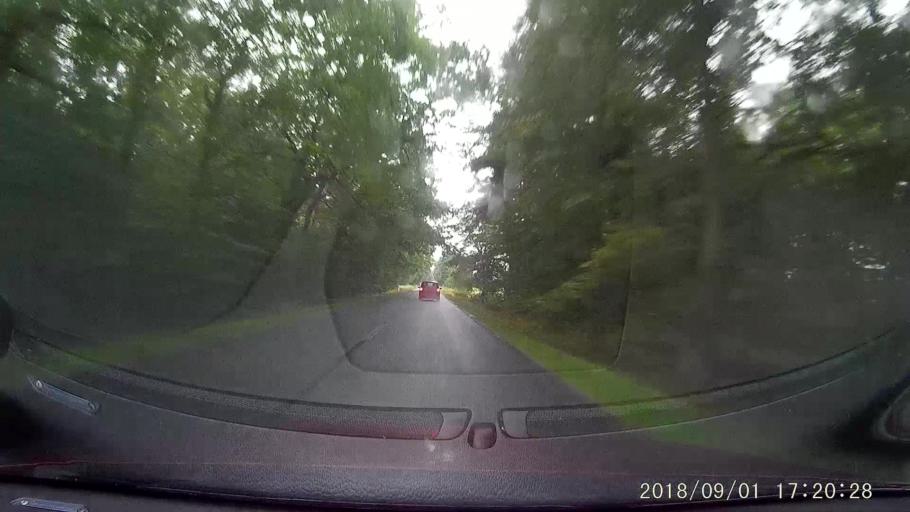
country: PL
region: Lubusz
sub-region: Powiat zielonogorski
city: Nowogrod Bobrzanski
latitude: 51.7241
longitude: 15.2794
